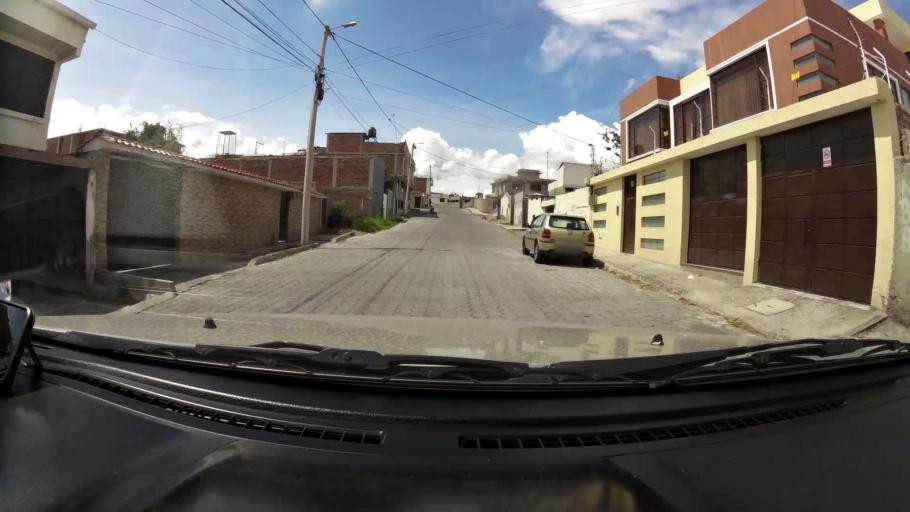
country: EC
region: Chimborazo
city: Riobamba
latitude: -1.6577
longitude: -78.6409
